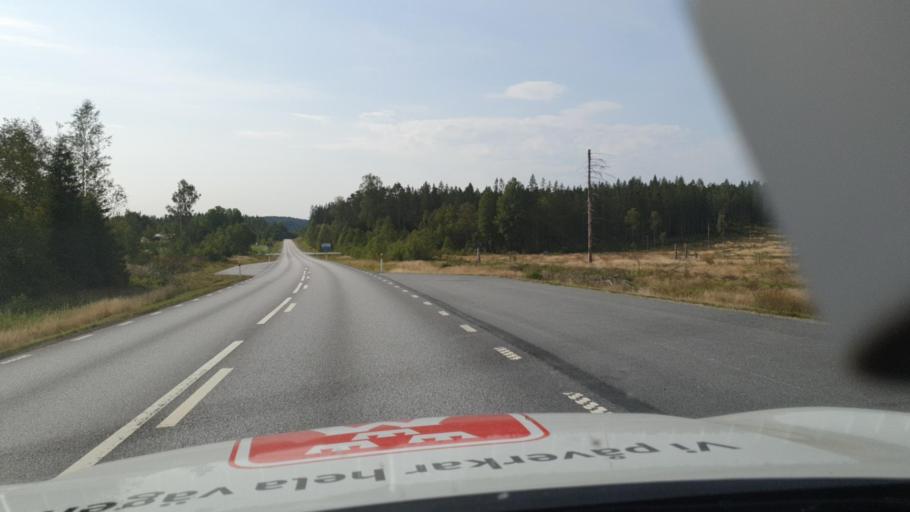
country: SE
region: Vaestra Goetaland
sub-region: Tanums Kommun
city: Tanumshede
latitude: 58.8307
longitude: 11.6103
